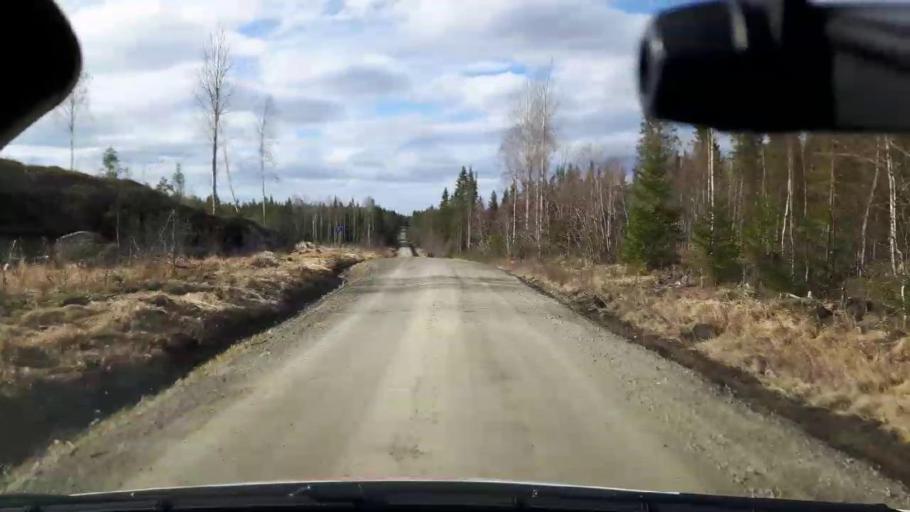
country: SE
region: Jaemtland
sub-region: Bergs Kommun
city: Hoverberg
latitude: 62.8589
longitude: 14.6676
